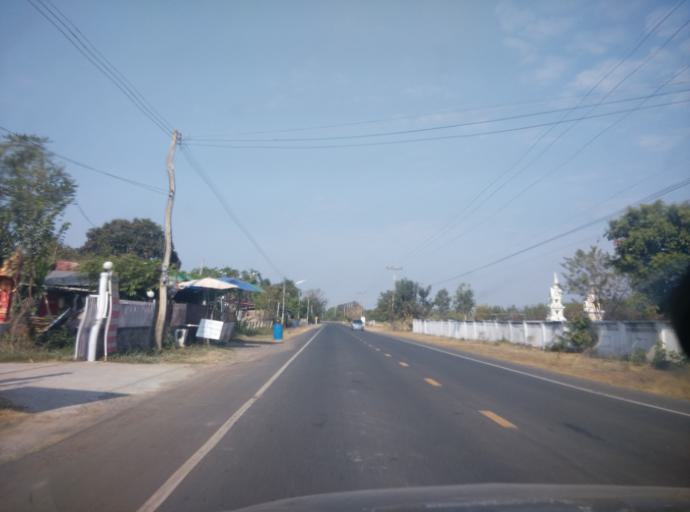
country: TH
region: Sisaket
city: Si Sa Ket
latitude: 15.1156
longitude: 104.2622
